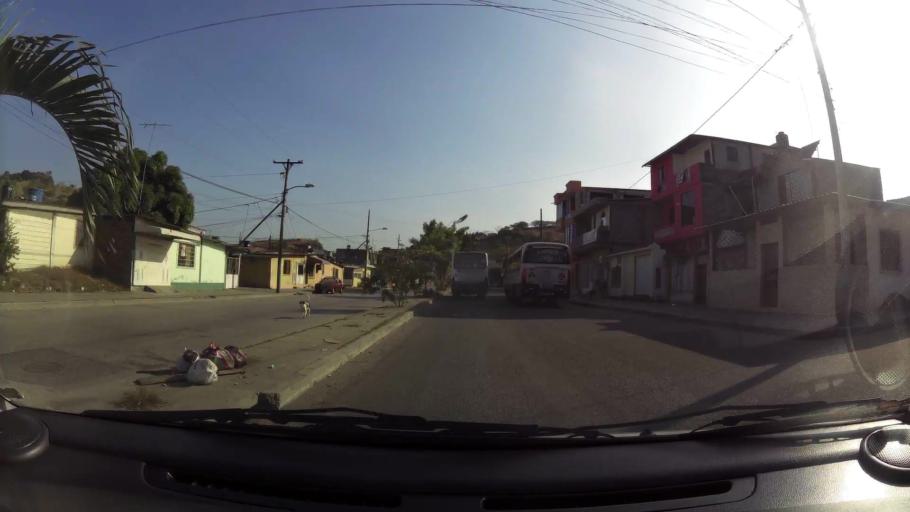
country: EC
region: Guayas
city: Eloy Alfaro
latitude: -2.1753
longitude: -79.8394
